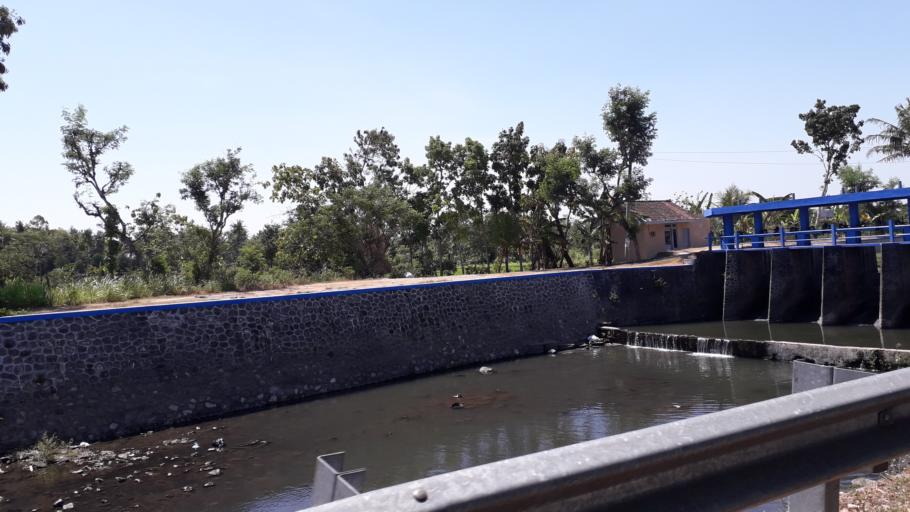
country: ID
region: Daerah Istimewa Yogyakarta
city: Pundong
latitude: -7.9538
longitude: 110.3258
